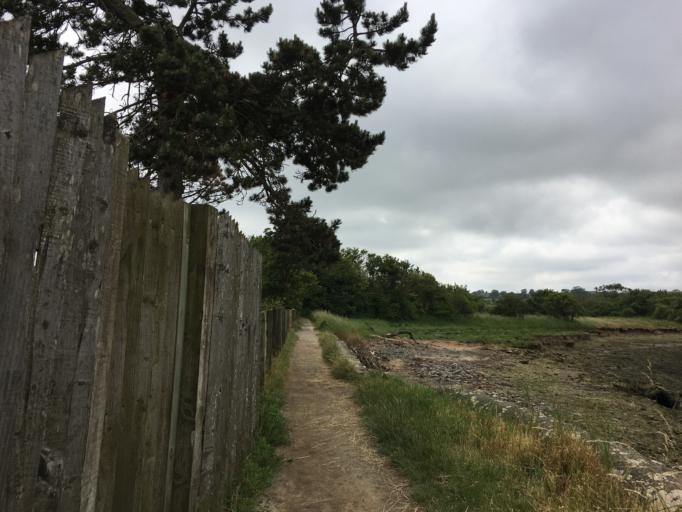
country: GB
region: England
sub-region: Northumberland
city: Alnmouth
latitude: 55.3892
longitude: -1.6174
